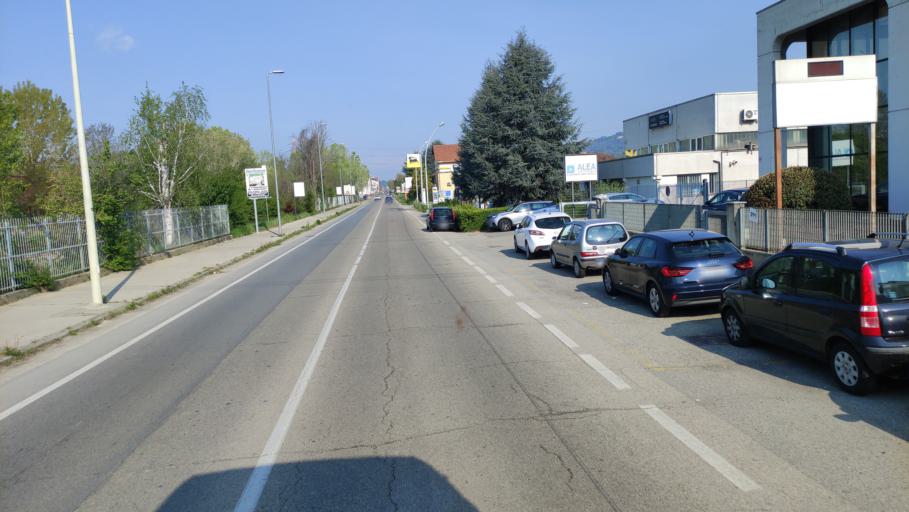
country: IT
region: Piedmont
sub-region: Provincia di Torino
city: Trofarello
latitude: 44.9874
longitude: 7.7270
